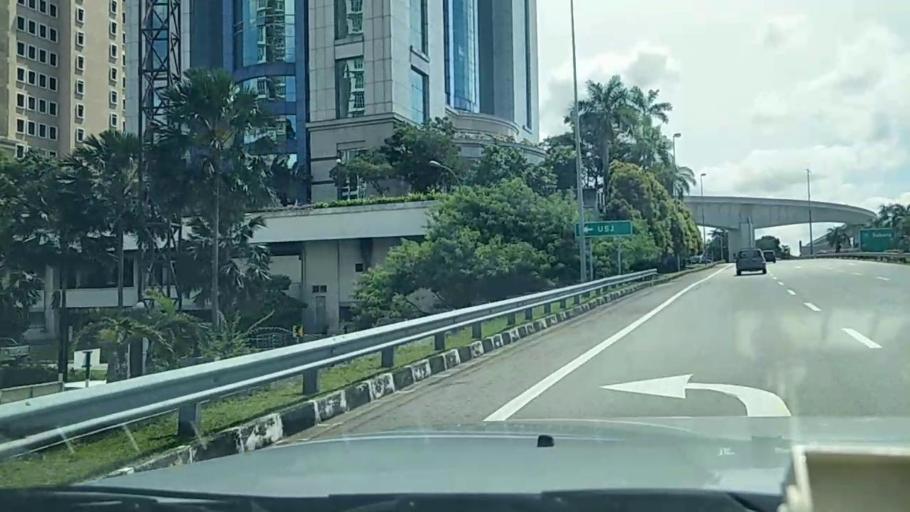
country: MY
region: Selangor
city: Subang Jaya
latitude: 3.0626
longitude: 101.5946
